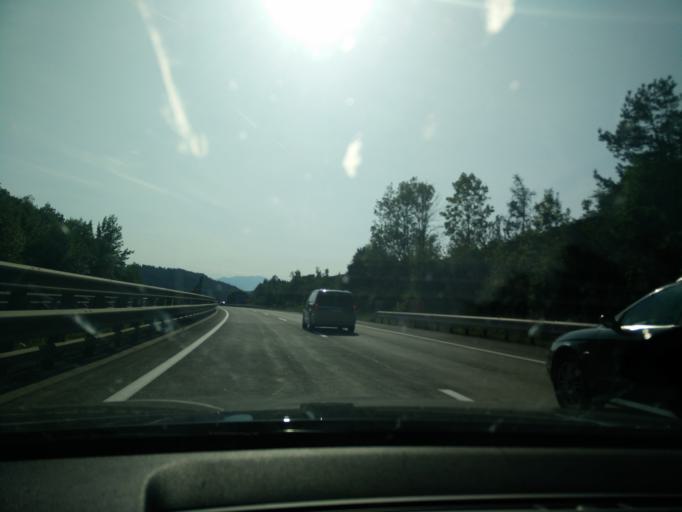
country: AT
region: Carinthia
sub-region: Politischer Bezirk Villach Land
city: Velden am Woerthersee
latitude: 46.6226
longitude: 14.0390
